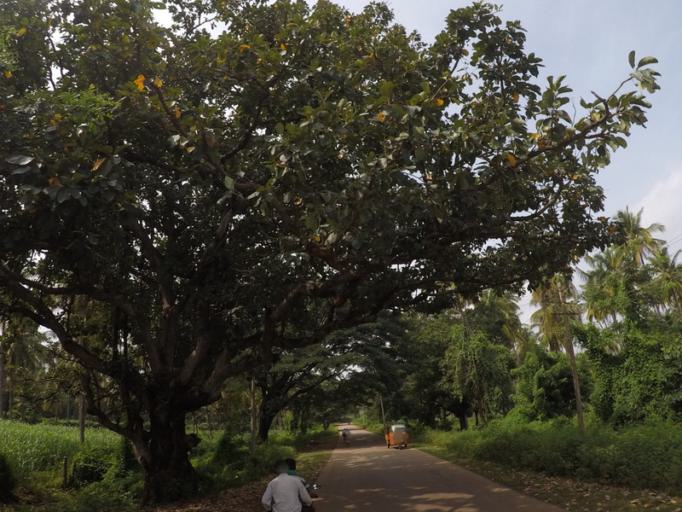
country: IN
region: Karnataka
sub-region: Chikmagalur
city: Tarikere
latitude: 13.5920
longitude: 75.8348
